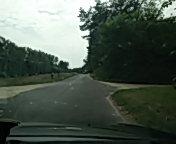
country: HU
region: Hajdu-Bihar
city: Hajdusamson
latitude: 47.5009
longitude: 21.7344
